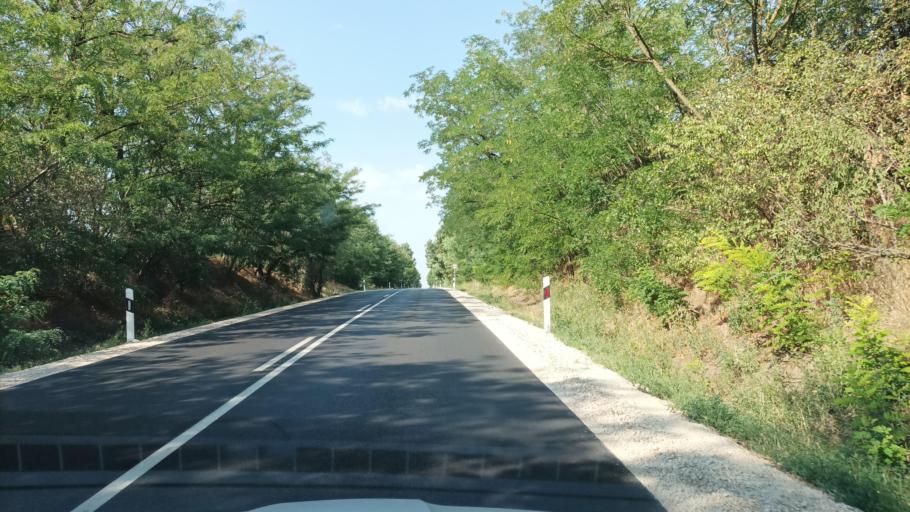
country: HU
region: Pest
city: Gomba
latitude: 47.3654
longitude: 19.5005
